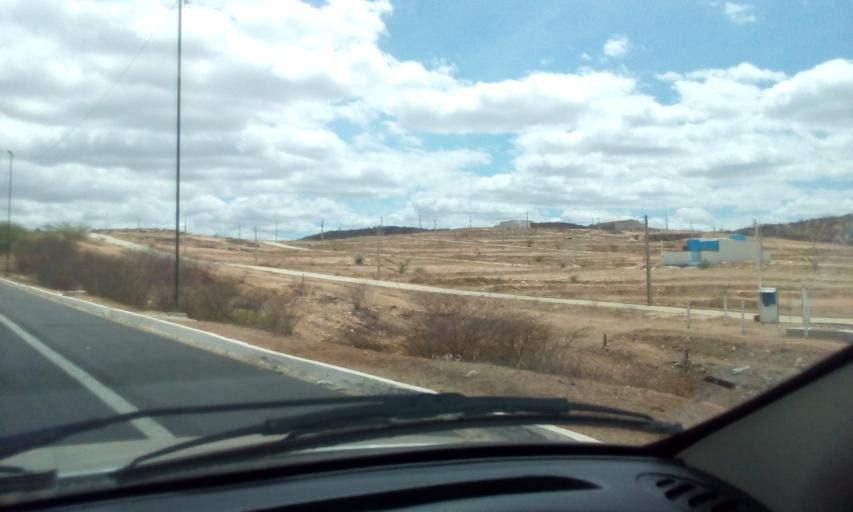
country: BR
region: Rio Grande do Norte
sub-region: Currais Novos
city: Currais Novos
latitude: -6.2581
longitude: -36.5004
